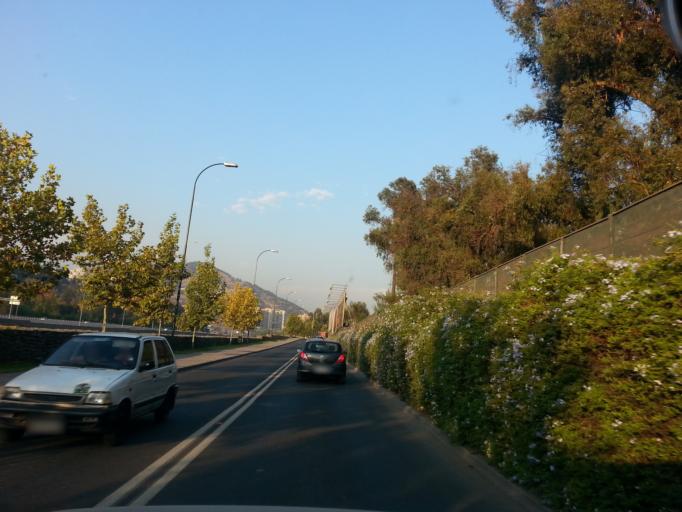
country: CL
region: Santiago Metropolitan
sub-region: Provincia de Santiago
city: Villa Presidente Frei, Nunoa, Santiago, Chile
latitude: -33.3773
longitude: -70.5598
